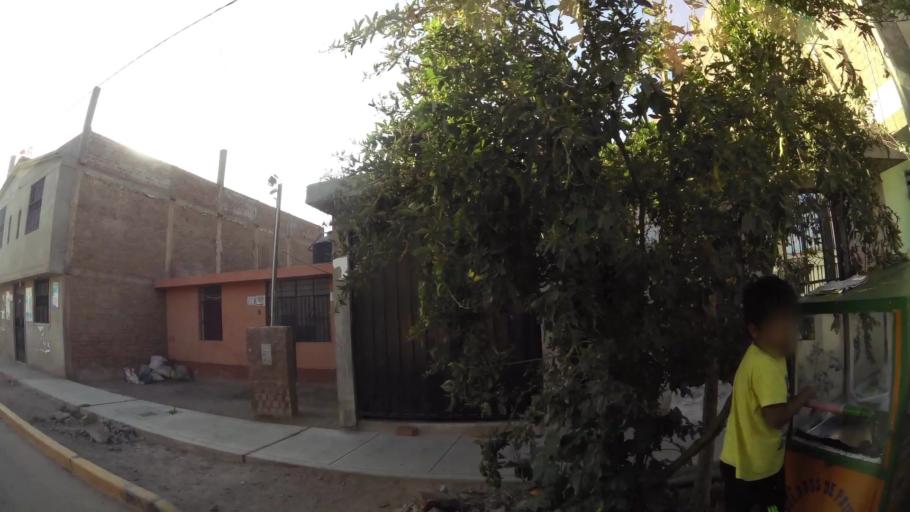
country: PE
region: Ica
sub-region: Provincia de Ica
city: Ica
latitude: -14.0676
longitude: -75.7175
